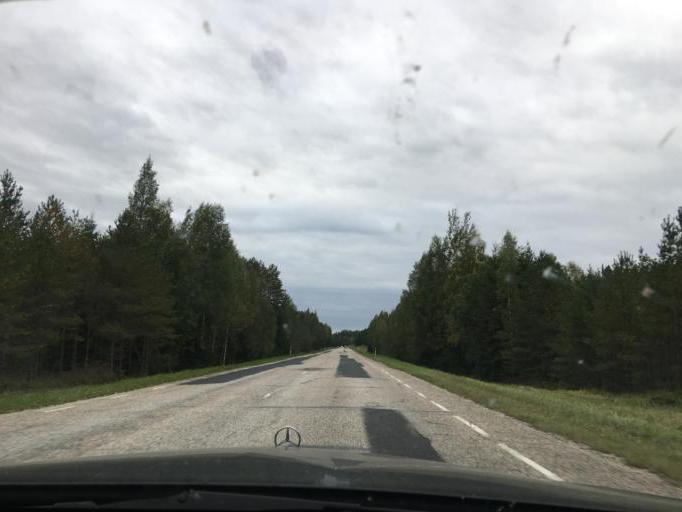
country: LV
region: Aluksnes Rajons
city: Aluksne
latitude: 57.5991
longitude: 27.1222
